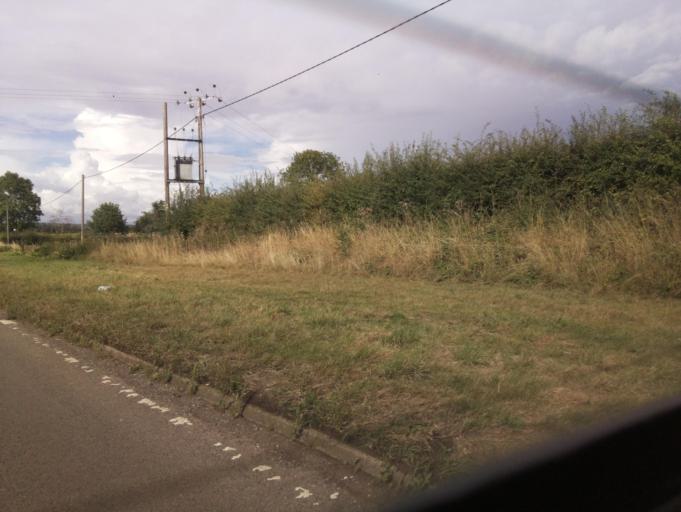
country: GB
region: England
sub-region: Telford and Wrekin
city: Madeley
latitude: 52.6112
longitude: -2.4111
